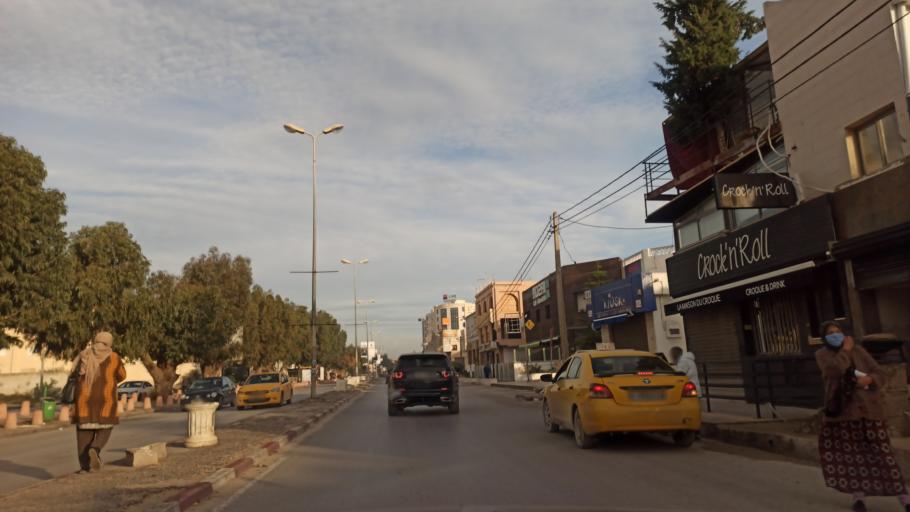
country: TN
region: Tunis
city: La Goulette
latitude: 36.8564
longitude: 10.2568
